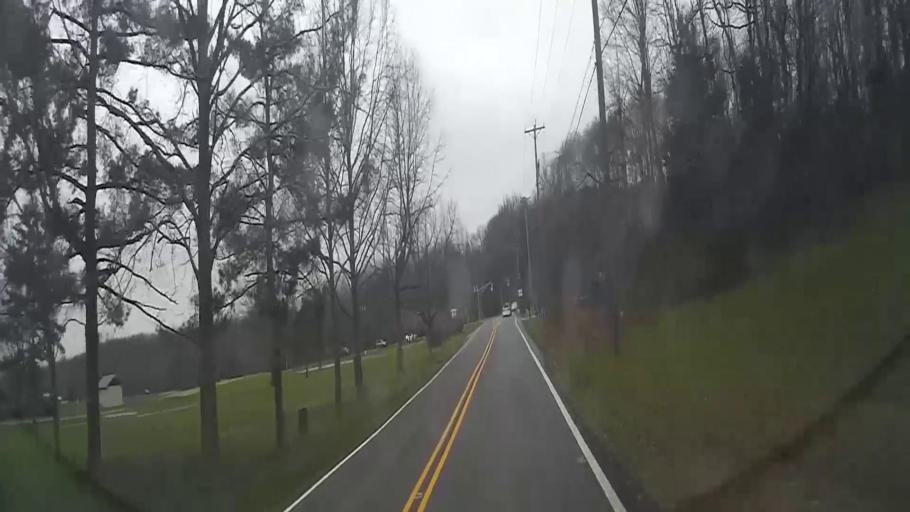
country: US
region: New Jersey
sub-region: Burlington County
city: Marlton
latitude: 39.8835
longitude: -74.8863
